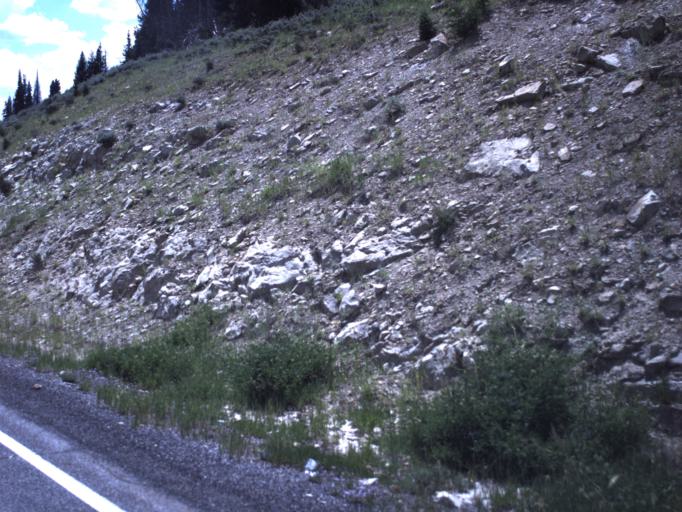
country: US
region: Utah
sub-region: Sanpete County
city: Fairview
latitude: 39.6832
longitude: -111.2456
